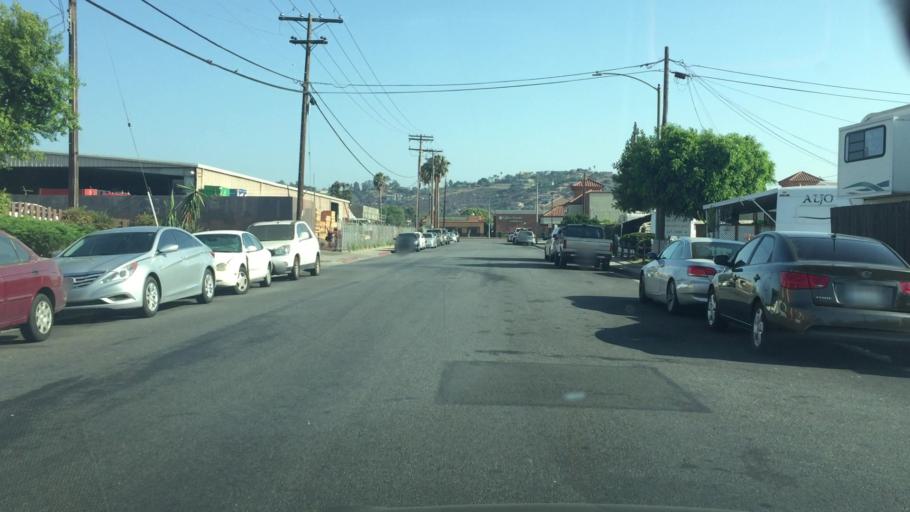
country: US
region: California
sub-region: San Diego County
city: Bostonia
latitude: 32.7968
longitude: -116.9380
